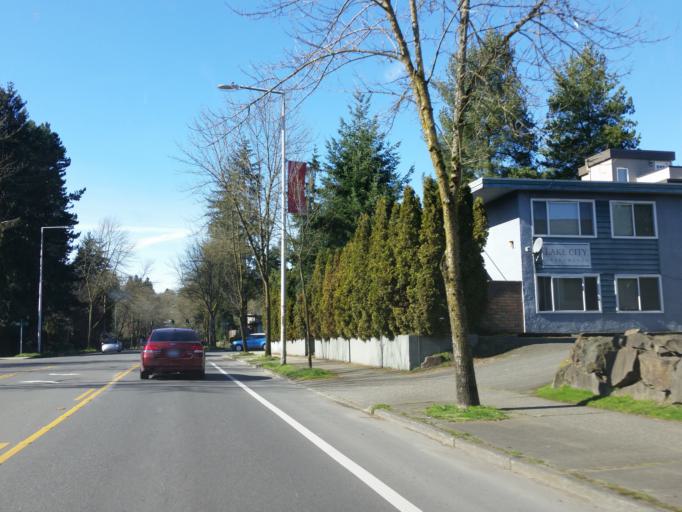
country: US
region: Washington
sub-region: King County
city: Lake Forest Park
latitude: 47.7195
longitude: -122.2995
